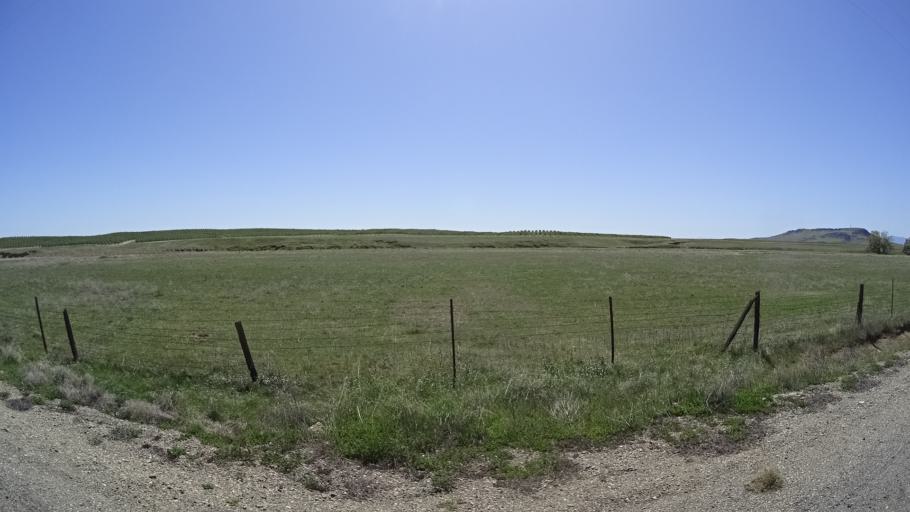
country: US
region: California
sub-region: Glenn County
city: Orland
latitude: 39.7809
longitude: -122.2986
